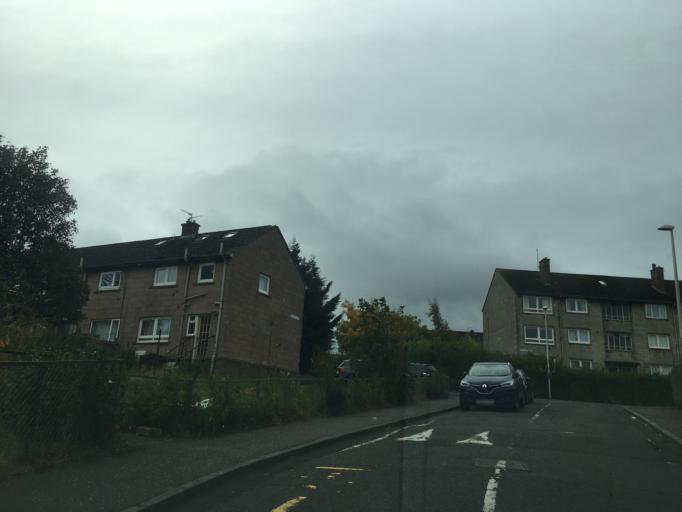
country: GB
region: Scotland
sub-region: Edinburgh
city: Colinton
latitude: 55.9080
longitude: -3.2227
